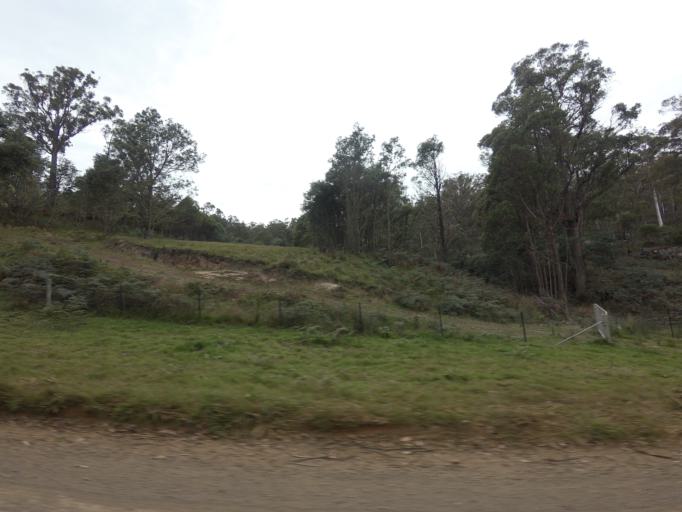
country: AU
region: Tasmania
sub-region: Derwent Valley
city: New Norfolk
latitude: -42.5819
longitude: 147.0076
